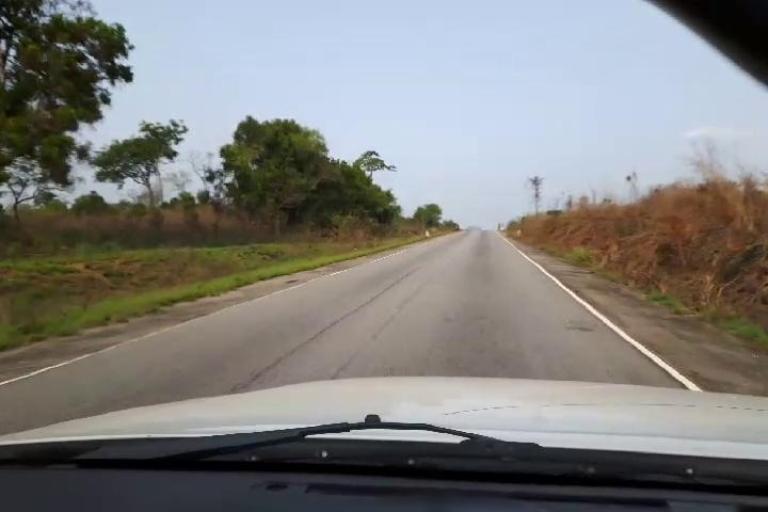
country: SL
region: Eastern Province
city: Blama
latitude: 7.9326
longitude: -11.5198
